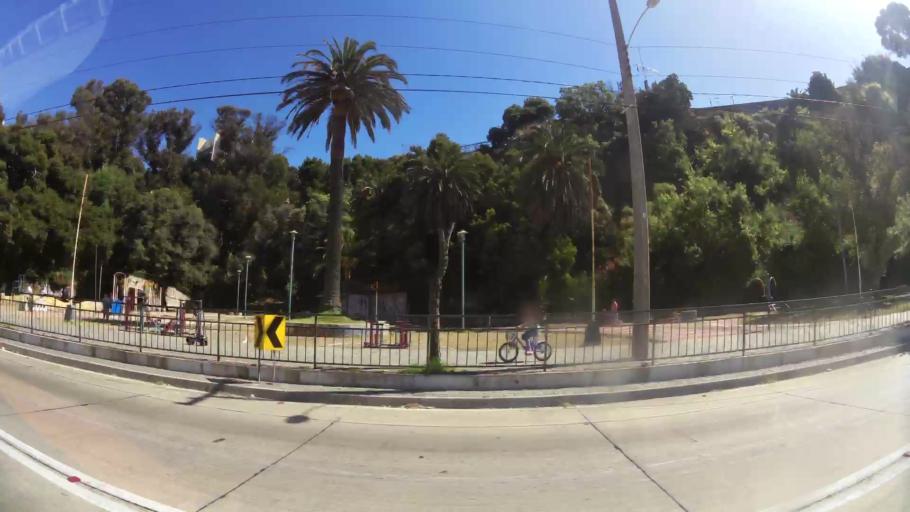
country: CL
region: Valparaiso
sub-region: Provincia de Valparaiso
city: Valparaiso
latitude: -33.0201
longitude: -71.6369
